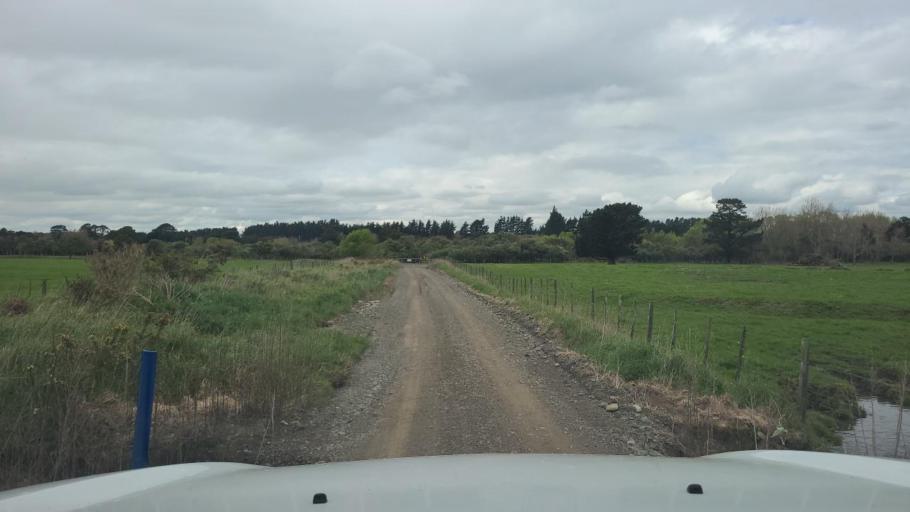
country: NZ
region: Wellington
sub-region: Upper Hutt City
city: Upper Hutt
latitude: -41.0812
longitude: 175.3616
